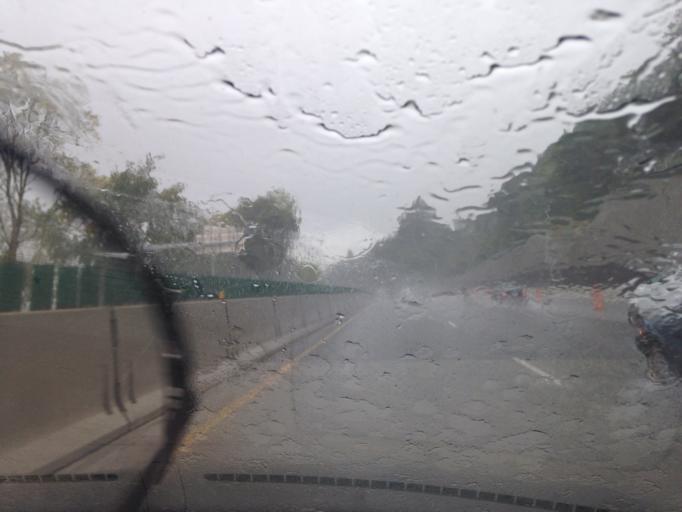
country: US
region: Oregon
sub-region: Multnomah County
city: Portland
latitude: 45.4789
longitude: -122.6789
